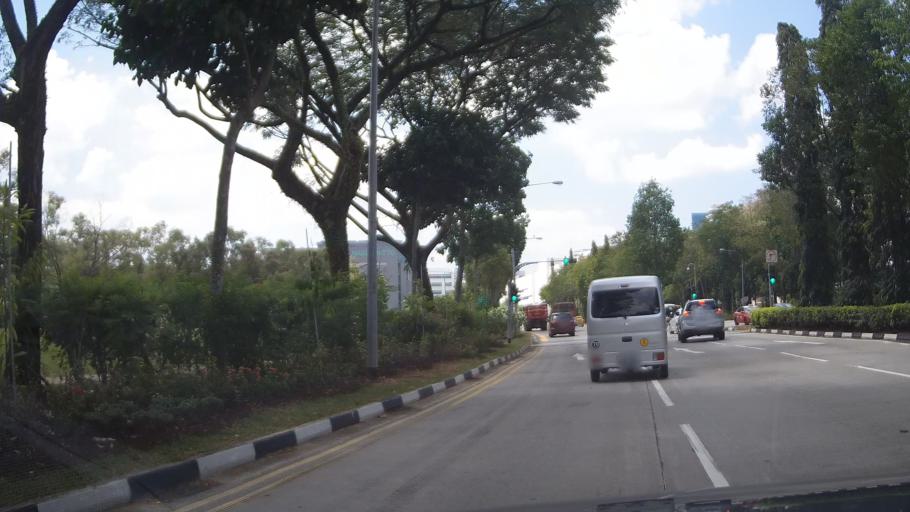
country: SG
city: Singapore
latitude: 1.3391
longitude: 103.7477
